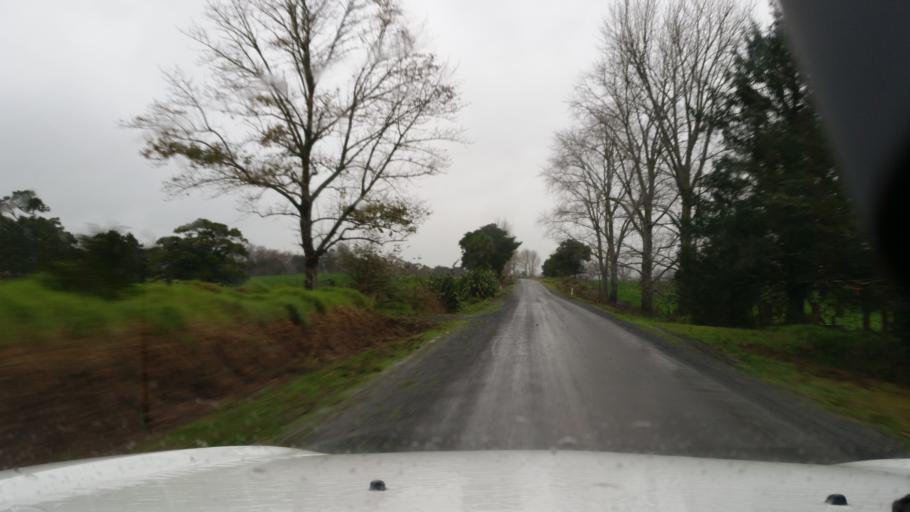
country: NZ
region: Northland
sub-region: Whangarei
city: Maungatapere
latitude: -35.7318
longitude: 174.0885
